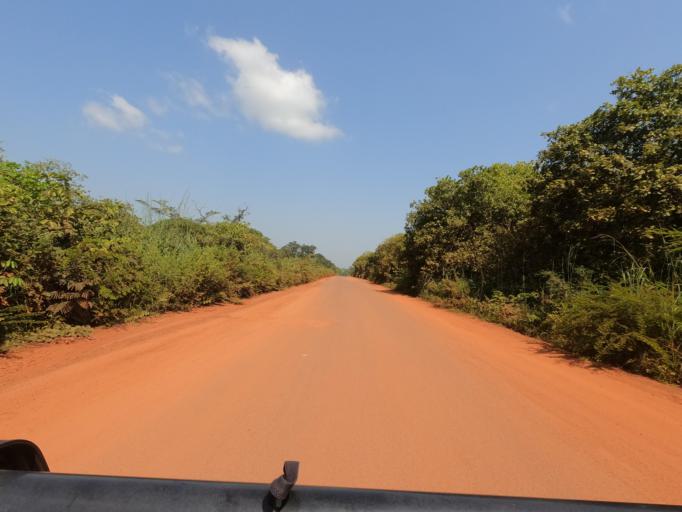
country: GW
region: Oio
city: Bissora
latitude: 12.3191
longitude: -15.7583
